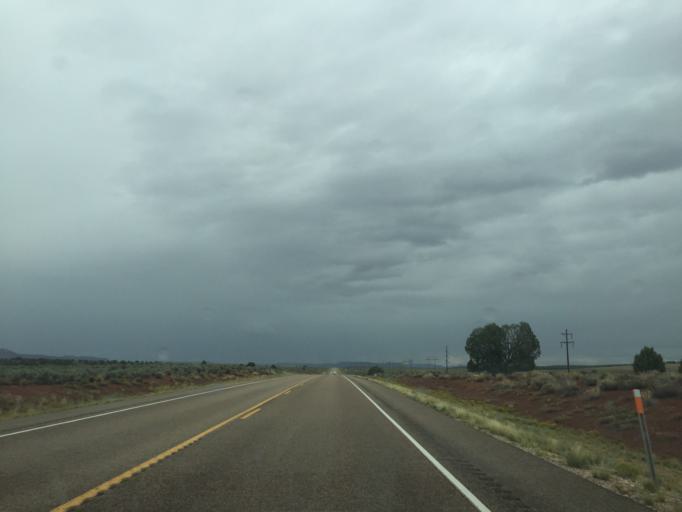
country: US
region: Utah
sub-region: Kane County
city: Kanab
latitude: 37.1447
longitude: -112.0699
